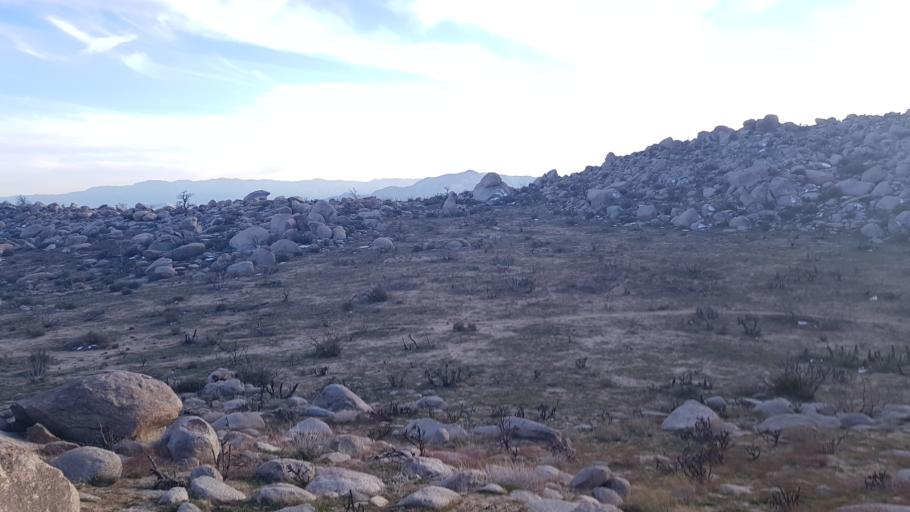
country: US
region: California
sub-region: San Diego County
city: Borrego Springs
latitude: 33.1787
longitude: -116.4314
